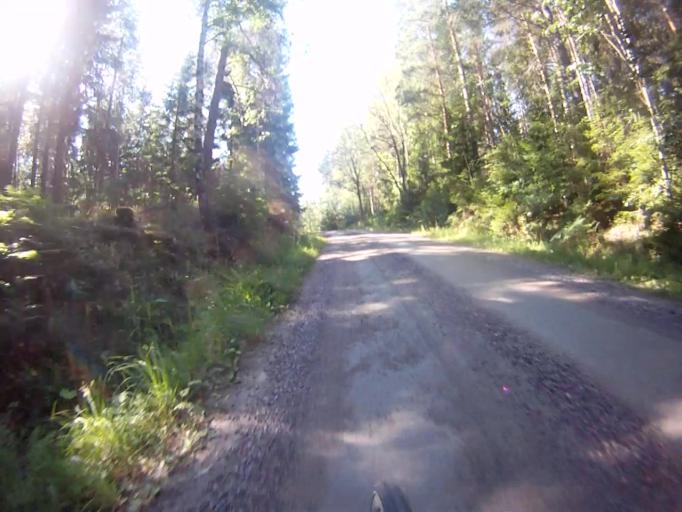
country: SE
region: Soedermanland
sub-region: Katrineholms Kommun
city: Katrineholm
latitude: 59.0652
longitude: 16.2757
